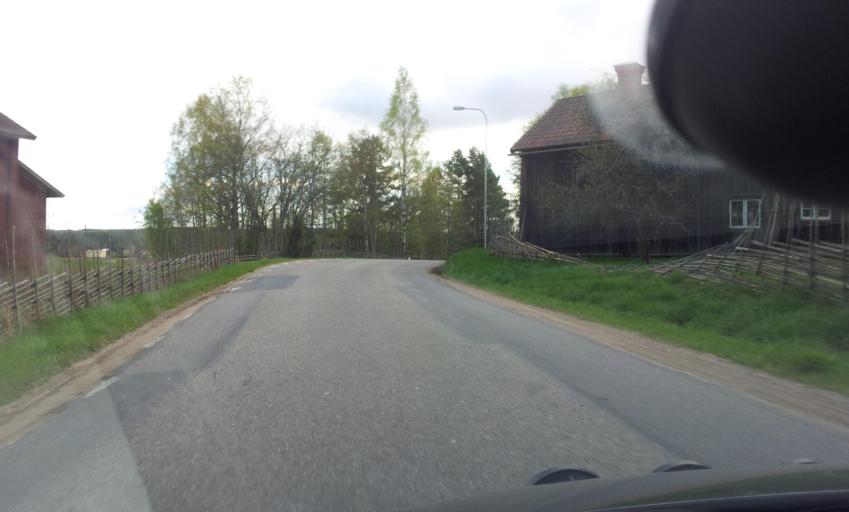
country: SE
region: Gaevleborg
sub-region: Bollnas Kommun
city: Kilafors
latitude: 61.3616
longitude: 16.5986
